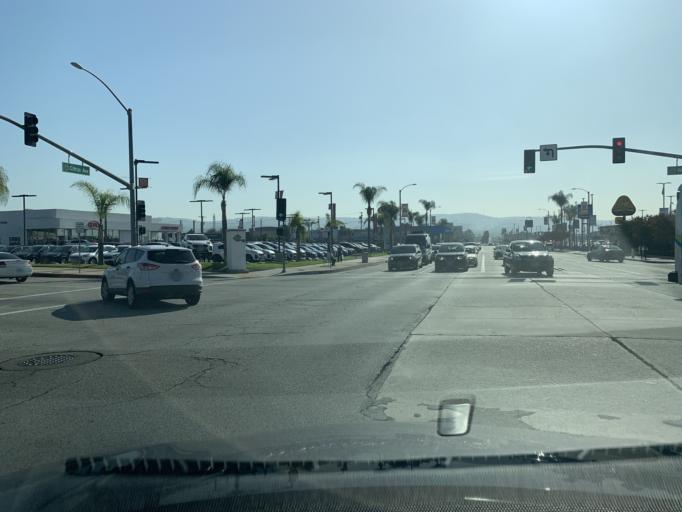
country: US
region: California
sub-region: Los Angeles County
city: Covina
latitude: 34.0791
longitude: -117.8901
